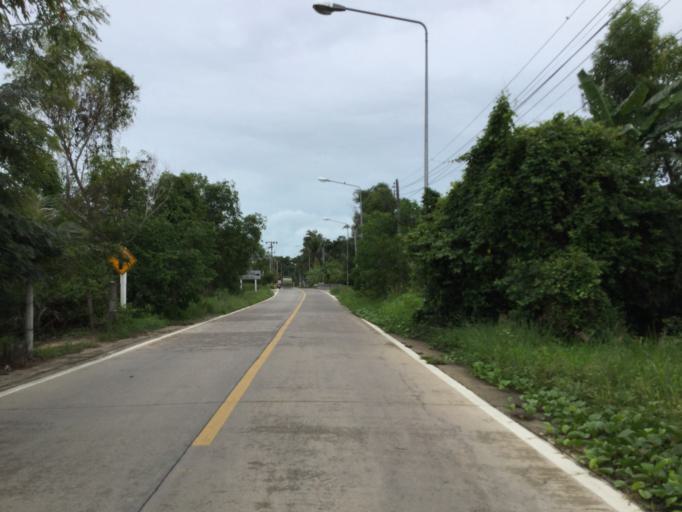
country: TH
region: Surat Thani
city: Ko Pha-Ngan
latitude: 9.7182
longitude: 100.0019
